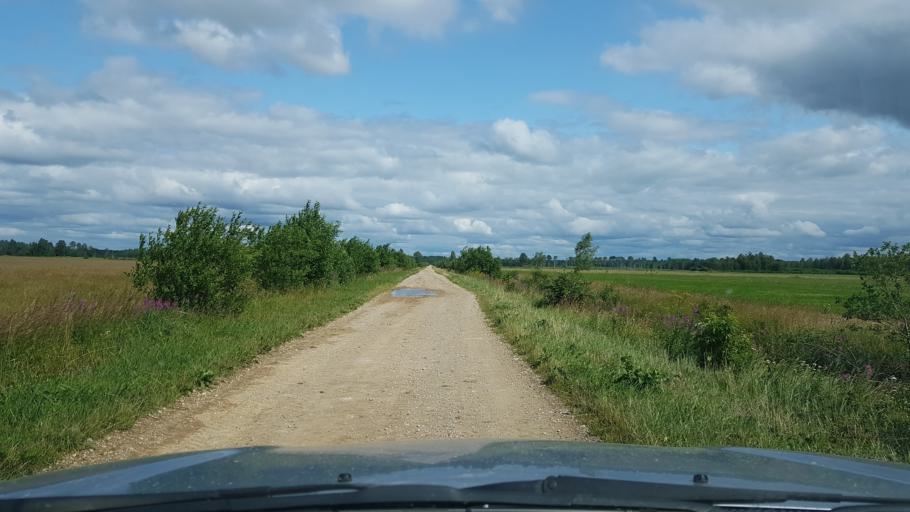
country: EE
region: Ida-Virumaa
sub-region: Sillamaee linn
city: Sillamae
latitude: 59.3703
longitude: 27.8981
